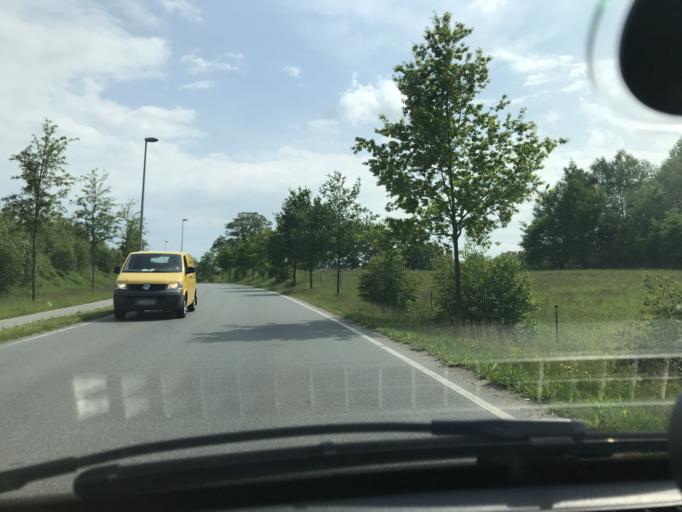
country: DE
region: Schleswig-Holstein
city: Trittau
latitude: 53.6122
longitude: 10.3934
